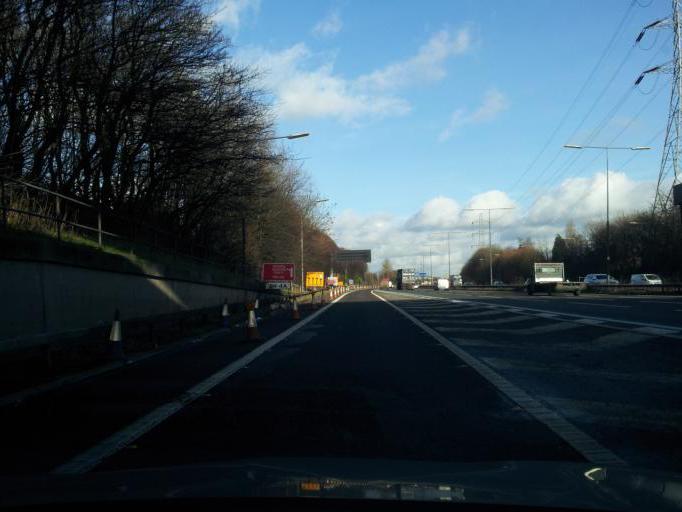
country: GB
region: England
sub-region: Borough of Bury
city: Prestwich
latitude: 53.5410
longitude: -2.2856
